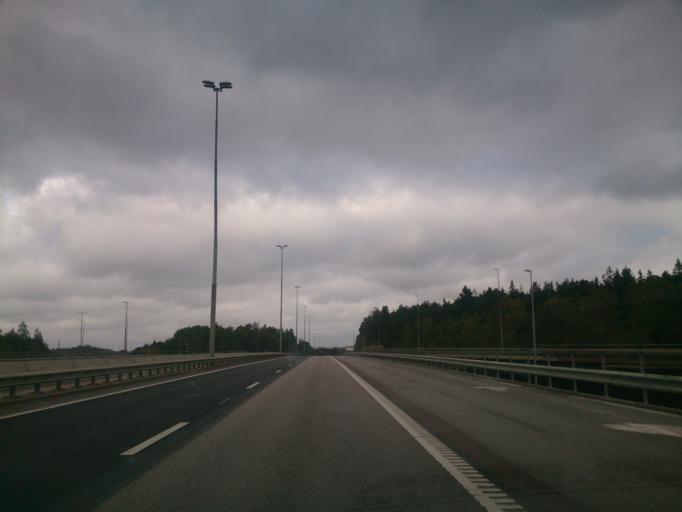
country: SE
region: Stockholm
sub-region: Haninge Kommun
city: Handen
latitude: 59.2292
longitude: 18.1253
